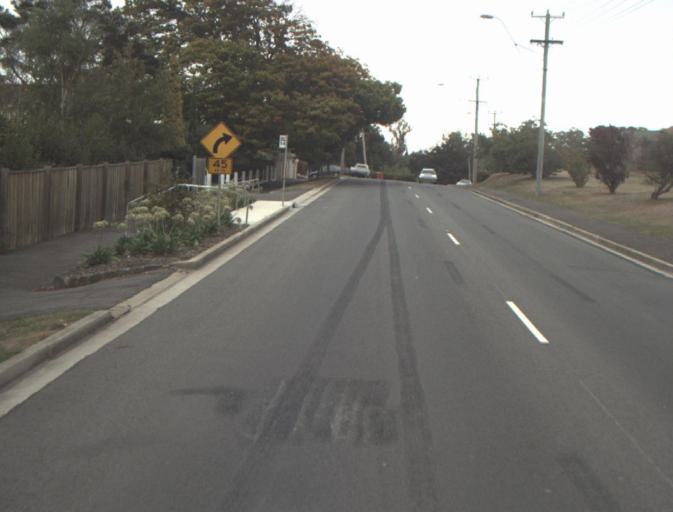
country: AU
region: Tasmania
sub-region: Launceston
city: West Launceston
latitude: -41.4625
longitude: 147.1502
